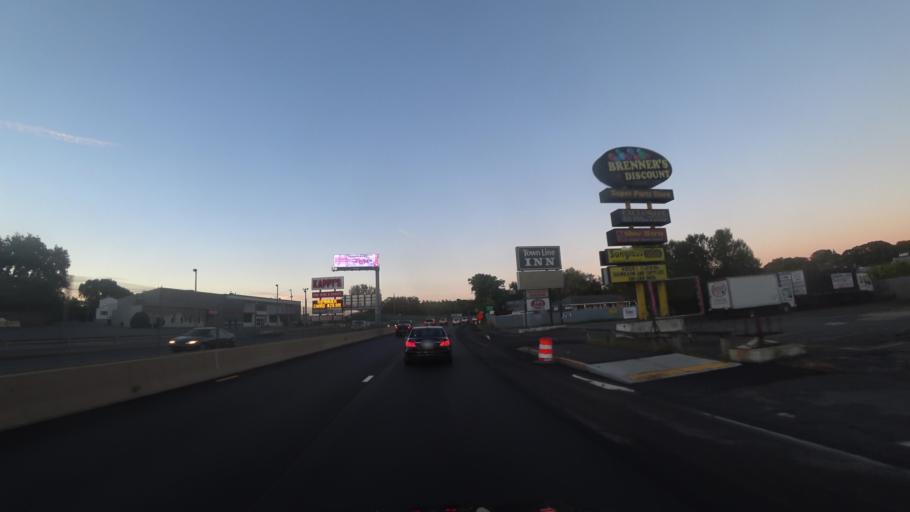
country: US
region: Massachusetts
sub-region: Essex County
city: Saugus
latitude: 42.4450
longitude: -71.0255
